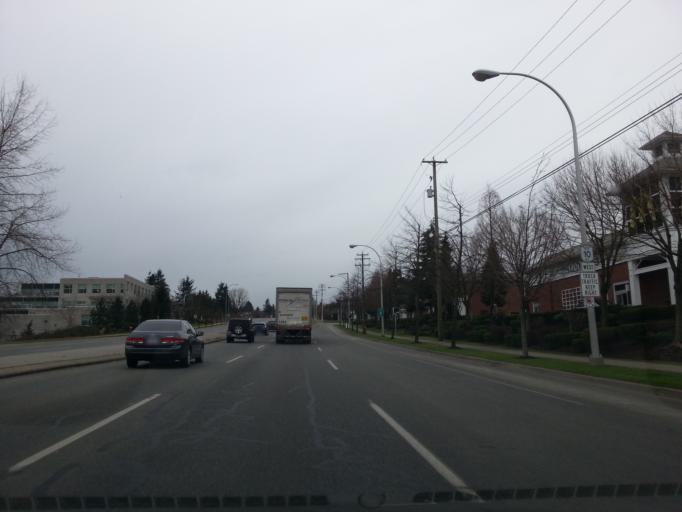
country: CA
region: British Columbia
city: Surrey
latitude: 49.1045
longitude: -122.8039
